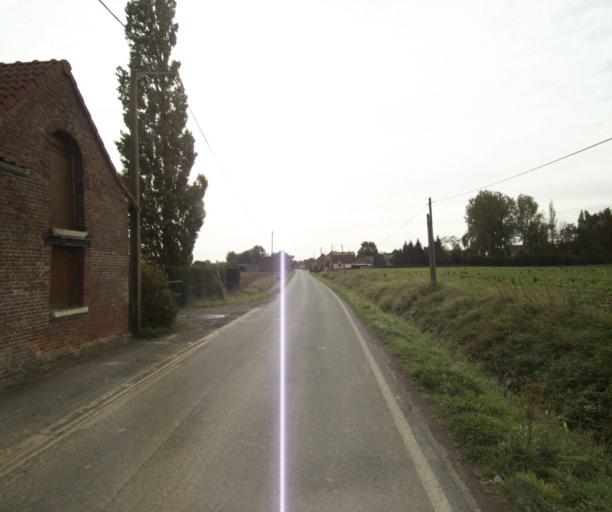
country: FR
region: Nord-Pas-de-Calais
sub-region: Departement du Nord
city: Fournes-en-Weppes
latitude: 50.6009
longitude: 2.8688
